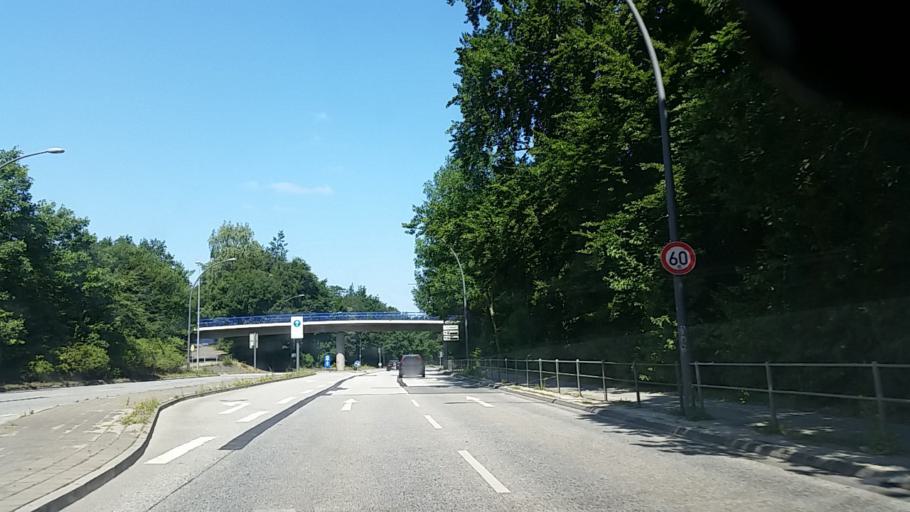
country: DE
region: Hamburg
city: Eidelstedt
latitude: 53.5851
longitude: 9.9078
